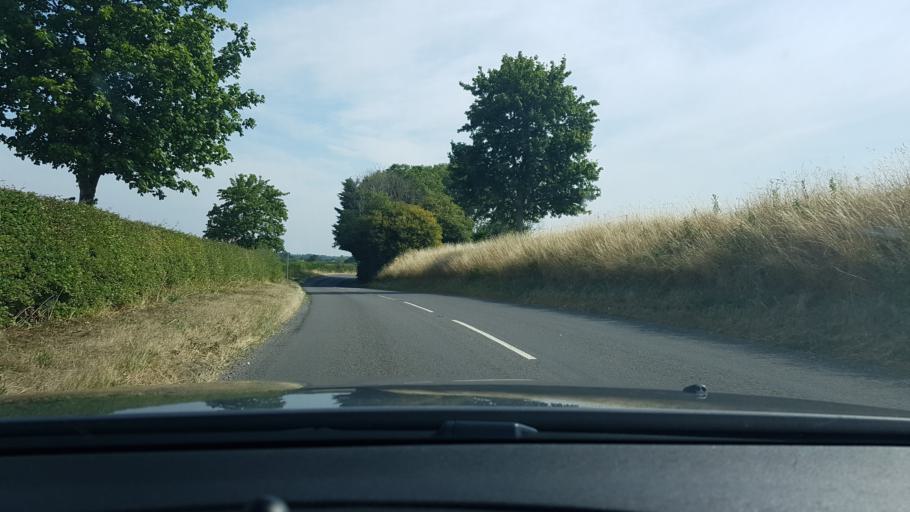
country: GB
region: England
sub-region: Wiltshire
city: Shalbourne
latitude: 51.3776
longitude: -1.5401
